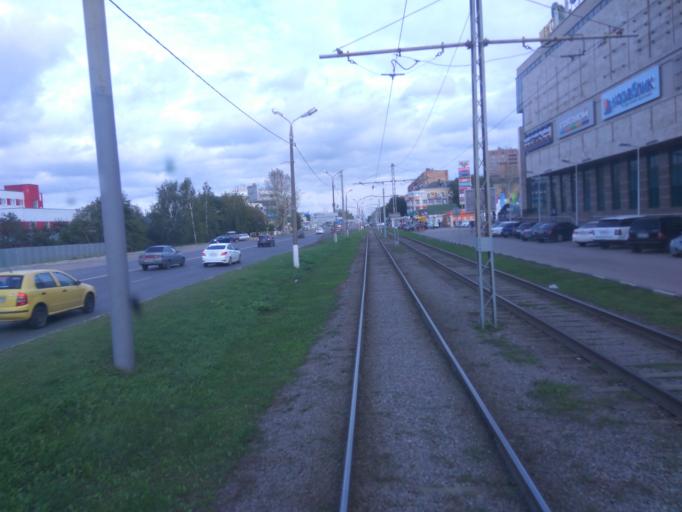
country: RU
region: Moskovskaya
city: Kolomna
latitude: 55.0849
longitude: 38.8001
